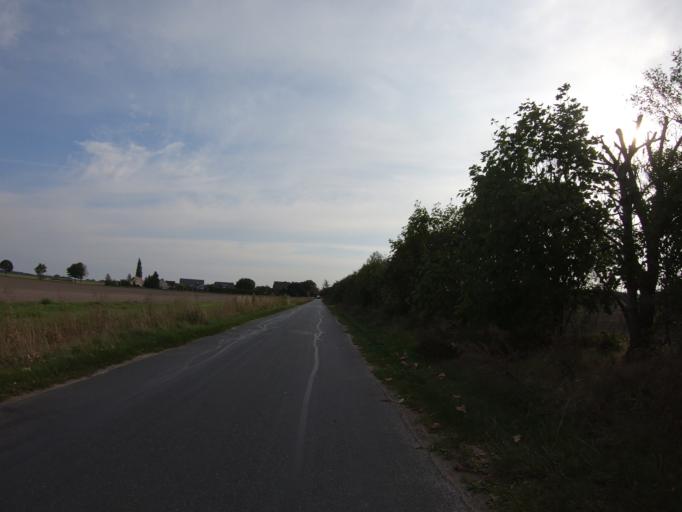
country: DE
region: Lower Saxony
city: Ribbesbuttel
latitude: 52.4385
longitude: 10.5136
